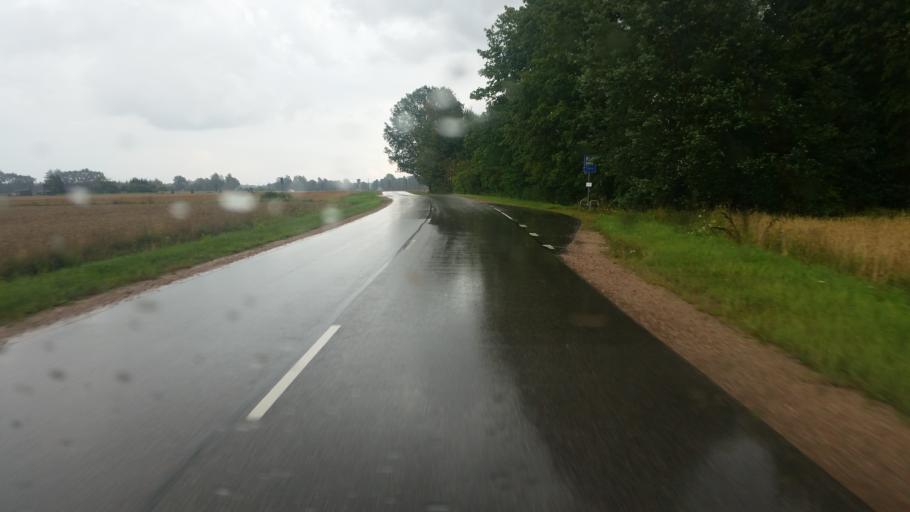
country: LV
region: Bauskas Rajons
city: Bauska
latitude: 56.4302
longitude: 24.3953
